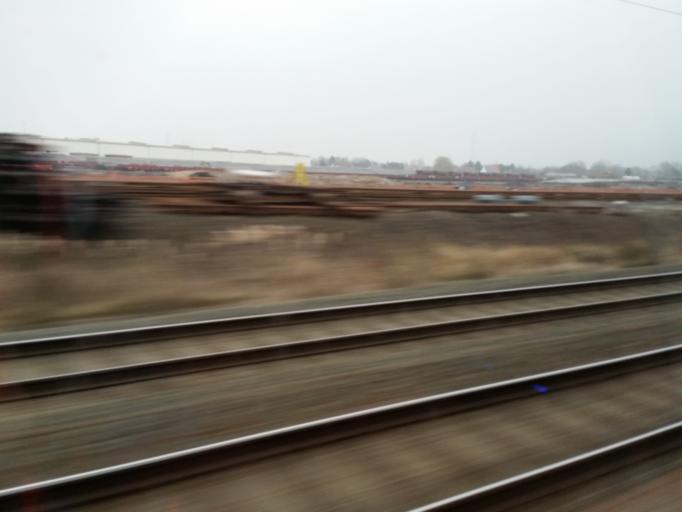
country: BE
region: Flanders
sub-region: Provincie Oost-Vlaanderen
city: Melle
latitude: 51.0153
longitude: 3.7737
